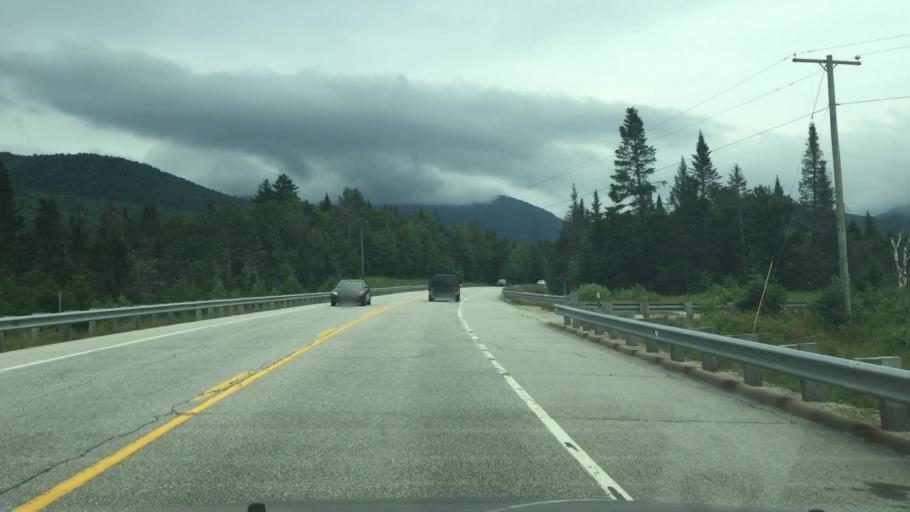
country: US
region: New Hampshire
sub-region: Coos County
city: Jefferson
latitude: 44.2380
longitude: -71.4242
